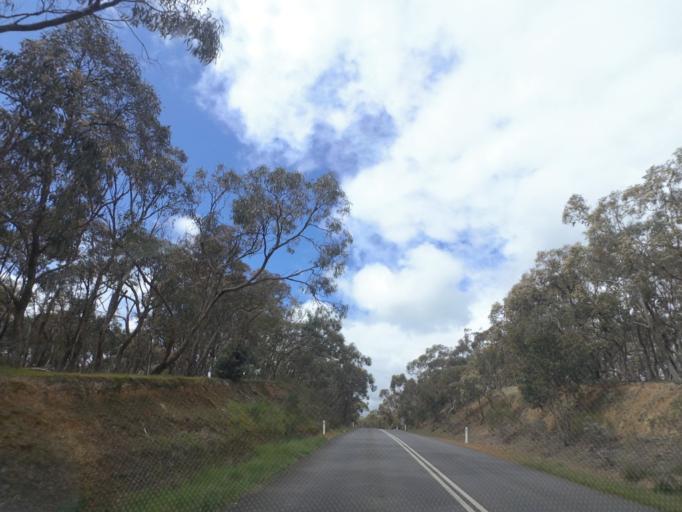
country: AU
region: Victoria
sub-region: Hume
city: Sunbury
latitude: -37.3576
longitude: 144.8095
